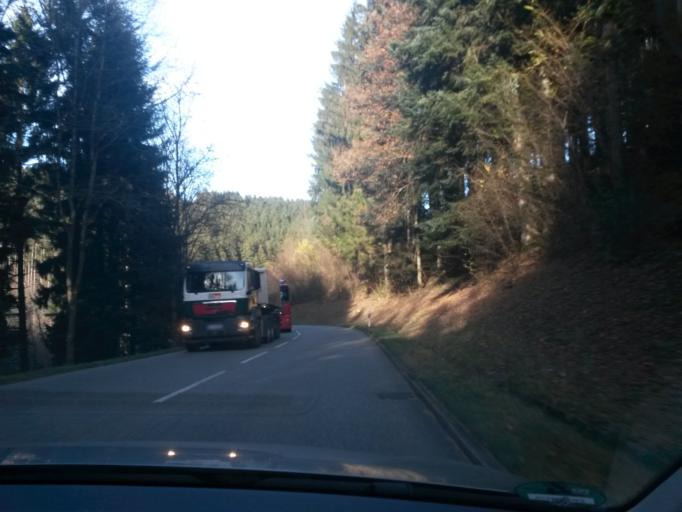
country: DE
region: Baden-Wuerttemberg
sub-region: Freiburg Region
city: Muhlenbach
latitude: 48.2233
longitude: 8.1006
